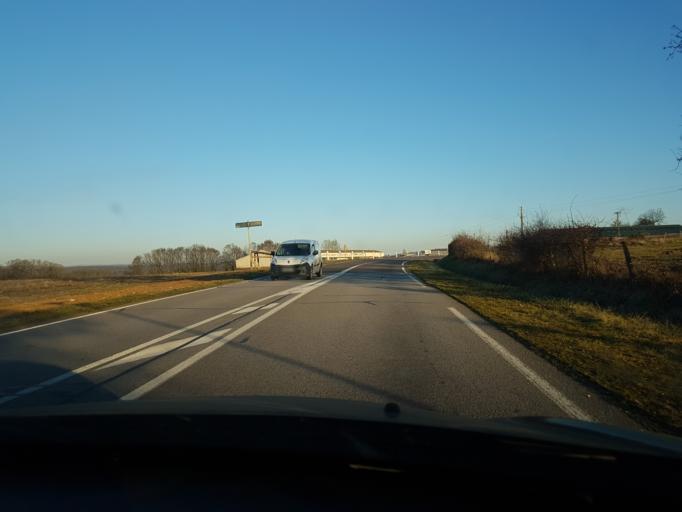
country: FR
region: Lorraine
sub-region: Departement des Vosges
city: Darney
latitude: 47.9302
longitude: 6.0826
